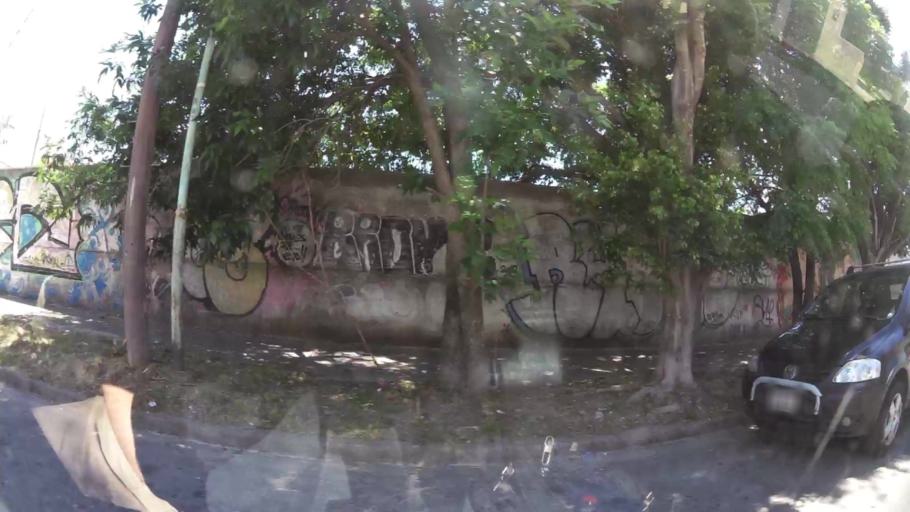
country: AR
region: Buenos Aires
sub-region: Partido de General San Martin
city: General San Martin
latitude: -34.5848
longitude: -58.5417
